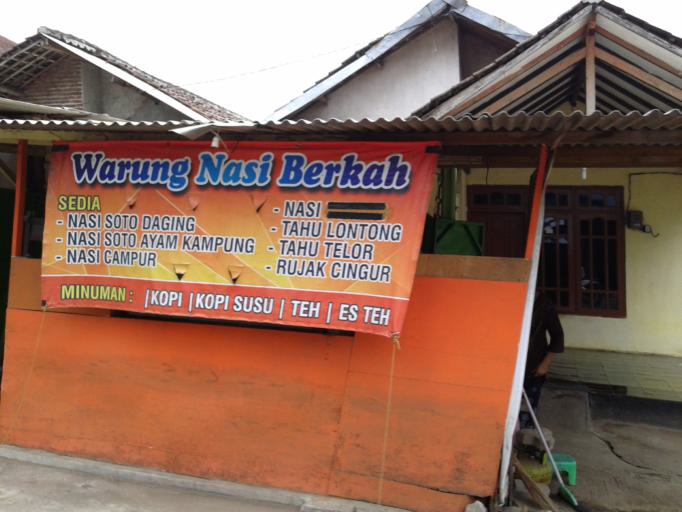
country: ID
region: East Java
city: Singosari
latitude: -7.8988
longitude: 112.6870
